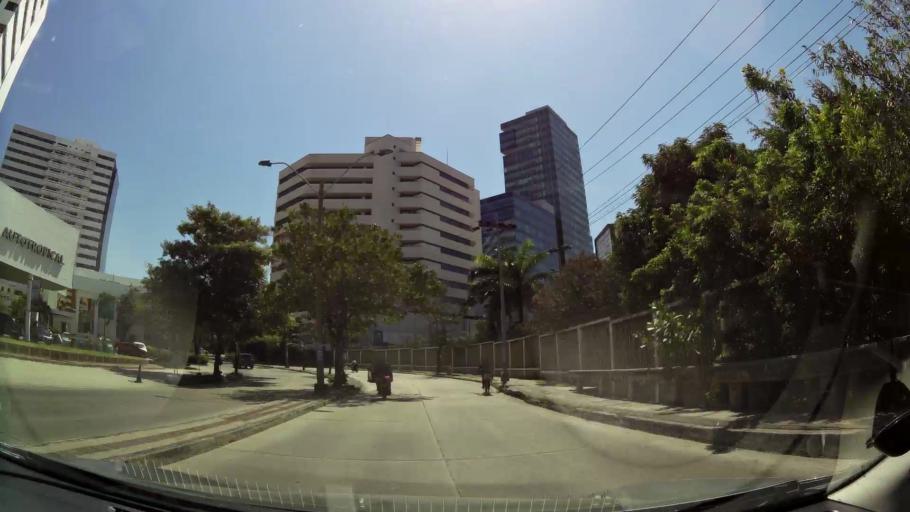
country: CO
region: Atlantico
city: Barranquilla
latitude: 11.0076
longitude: -74.8036
